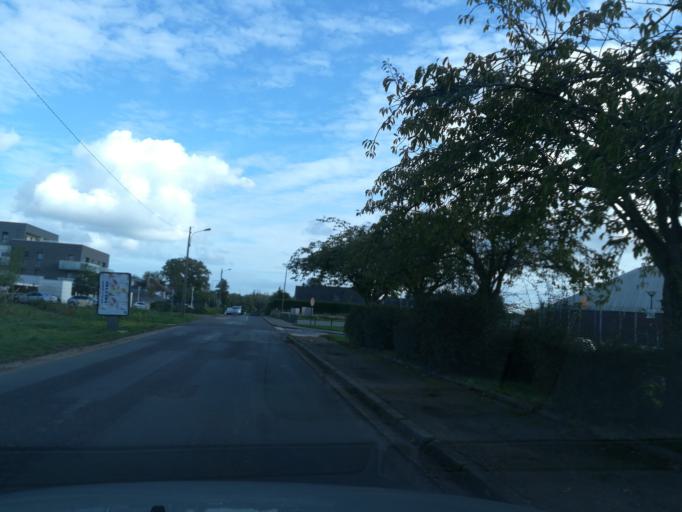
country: FR
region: Haute-Normandie
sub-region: Departement de la Seine-Maritime
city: Bois-Guillaume
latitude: 49.4727
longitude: 1.1280
